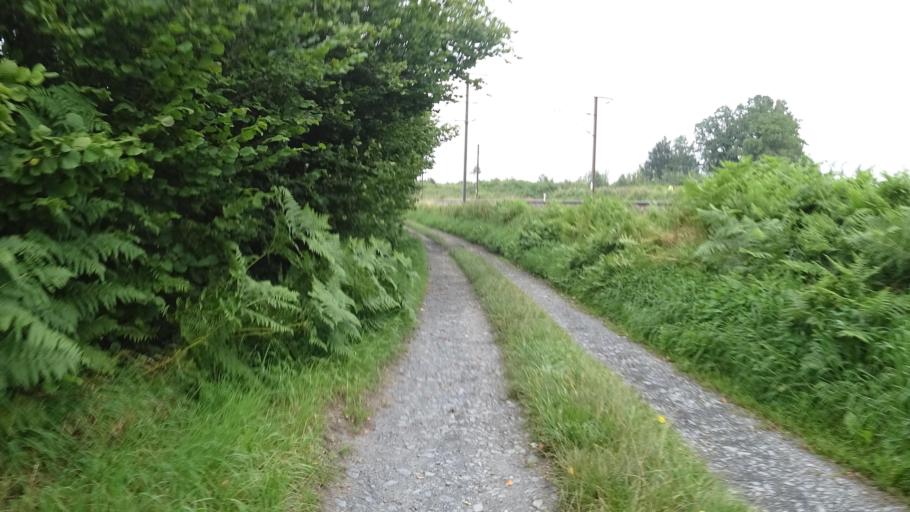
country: BE
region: Wallonia
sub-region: Province du Luxembourg
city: Chiny
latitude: 49.7973
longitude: 5.3314
